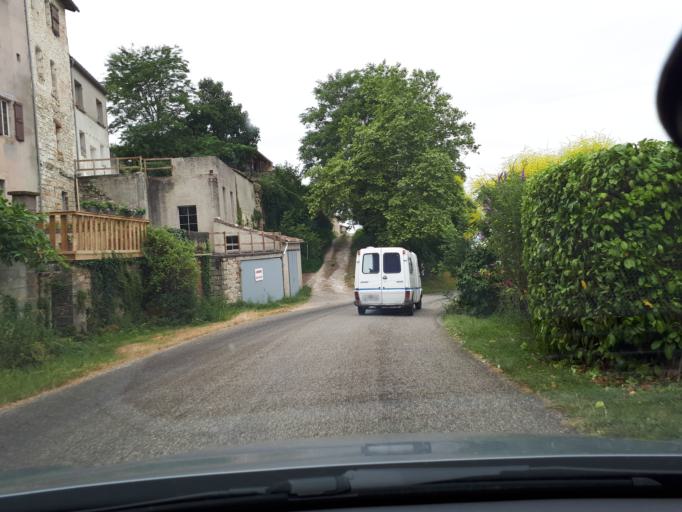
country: FR
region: Aquitaine
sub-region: Departement du Lot-et-Garonne
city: Astaffort
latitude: 43.9993
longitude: 0.7561
